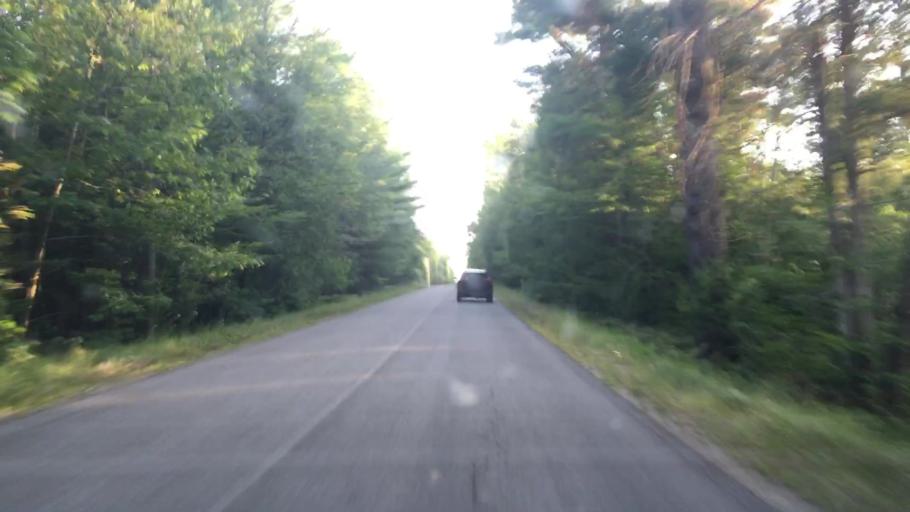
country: US
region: Maine
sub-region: Waldo County
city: Winterport
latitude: 44.6831
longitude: -68.9110
